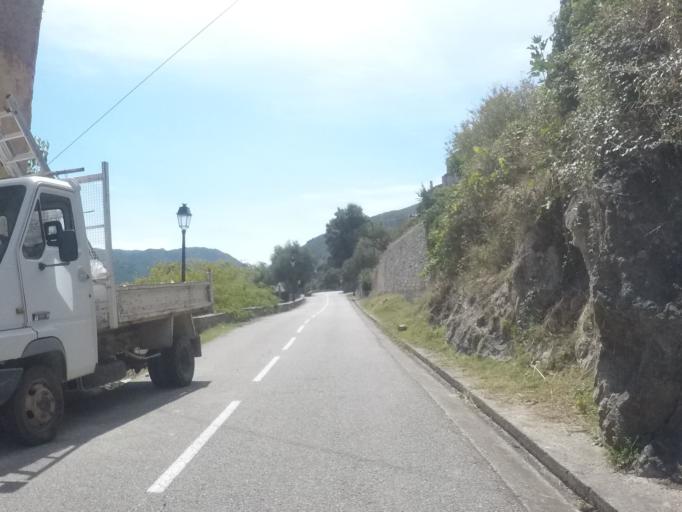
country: FR
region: Corsica
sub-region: Departement de la Haute-Corse
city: Corte
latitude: 42.3737
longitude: 9.1447
